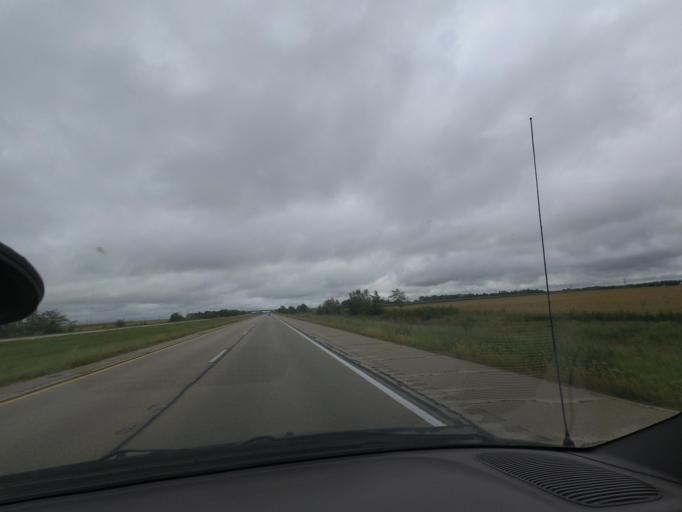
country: US
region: Illinois
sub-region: Piatt County
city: Monticello
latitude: 40.0220
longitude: -88.6972
